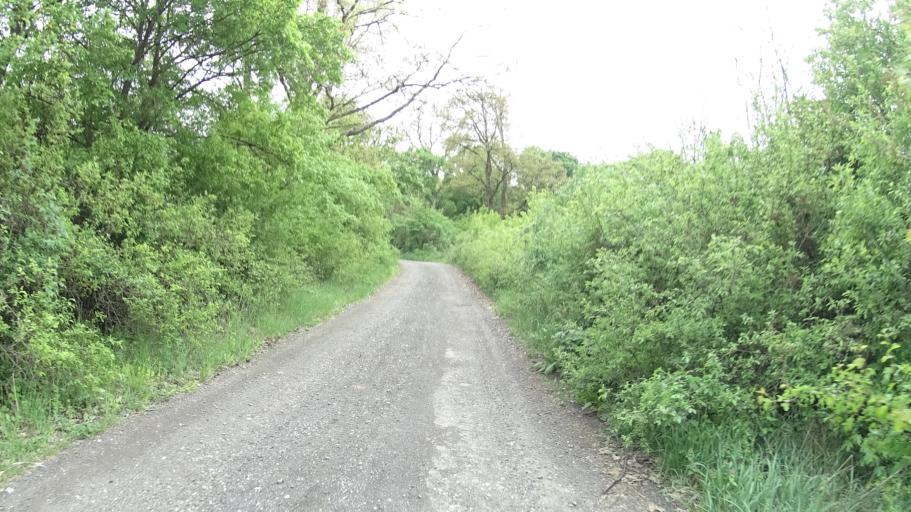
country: HU
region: Pest
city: Acsa
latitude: 47.8171
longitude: 19.3128
